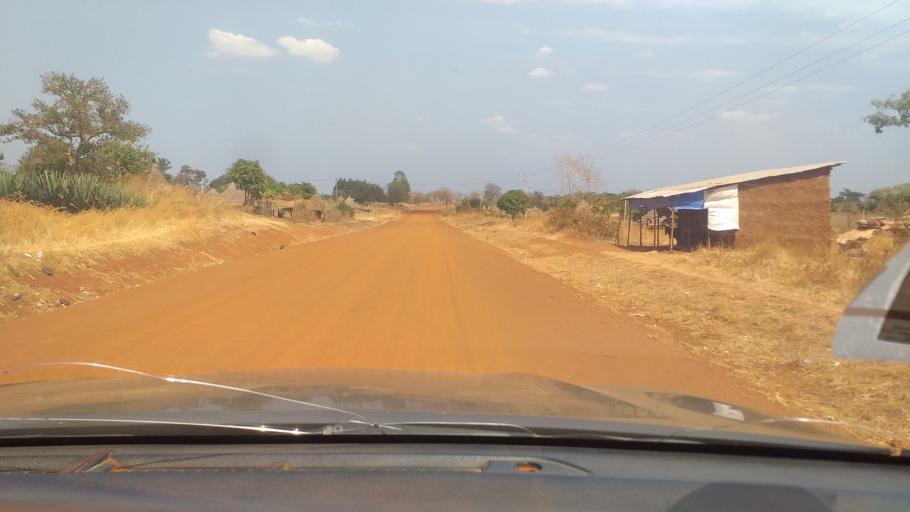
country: ET
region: Binshangul Gumuz
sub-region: Asosa
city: Asosa
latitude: 10.0621
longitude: 34.6963
